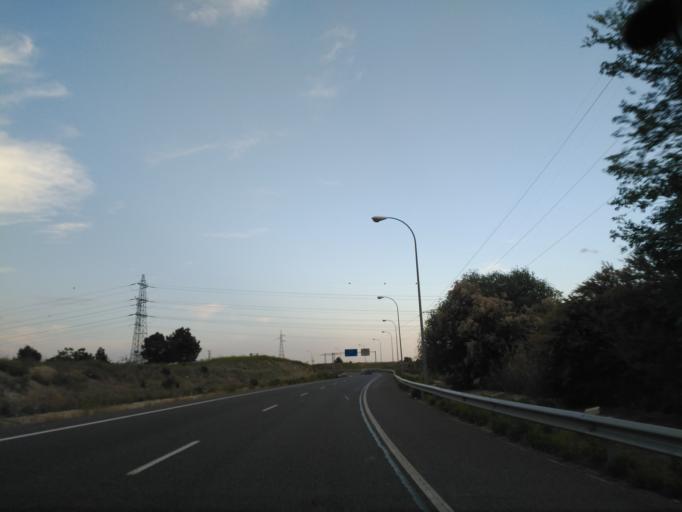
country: ES
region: Madrid
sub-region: Provincia de Madrid
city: Villaverde
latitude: 40.3321
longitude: -3.6753
